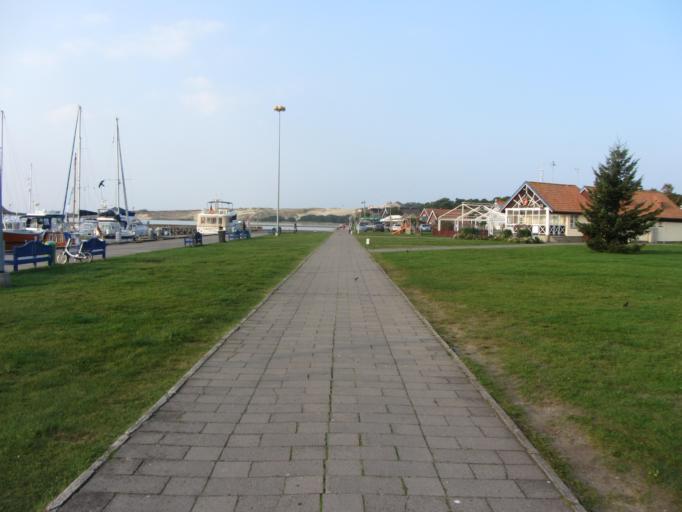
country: LT
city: Nida
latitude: 55.3027
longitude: 21.0086
